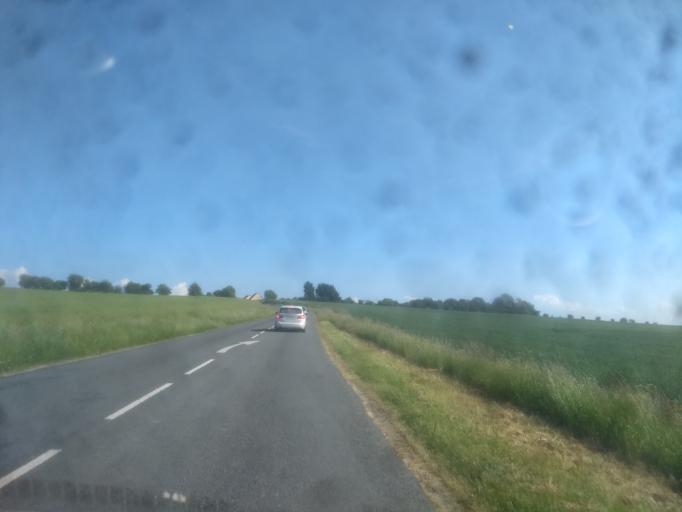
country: FR
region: Picardie
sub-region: Departement de la Somme
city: Saint-Riquier
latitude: 50.1416
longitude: 1.9407
